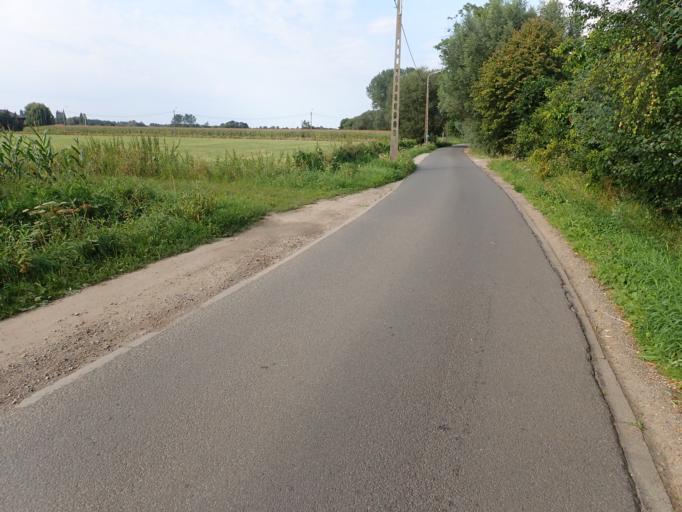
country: BE
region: Flanders
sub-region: Provincie Antwerpen
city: Sint-Amands
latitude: 51.0682
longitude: 4.2340
